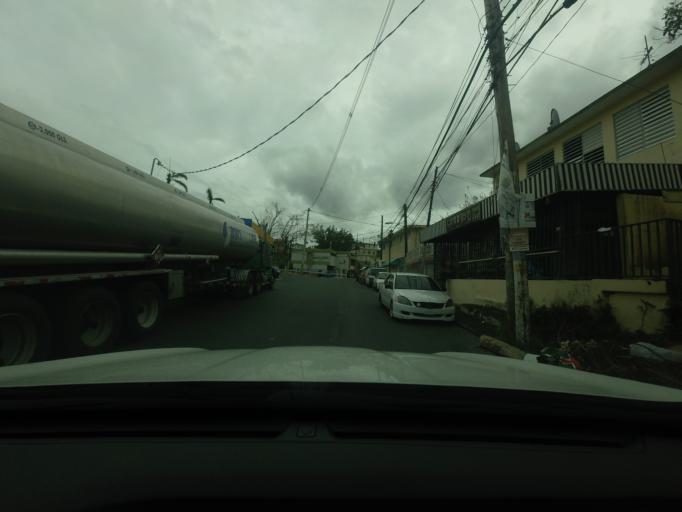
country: PR
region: Ciales
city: Ciales
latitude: 18.3410
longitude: -66.4684
